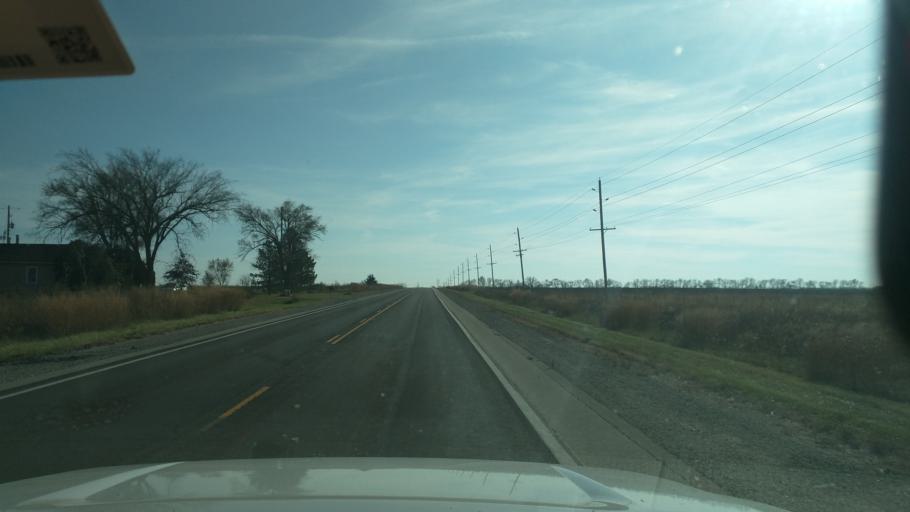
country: US
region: Kansas
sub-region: Lyon County
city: Emporia
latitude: 38.3019
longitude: -96.1804
